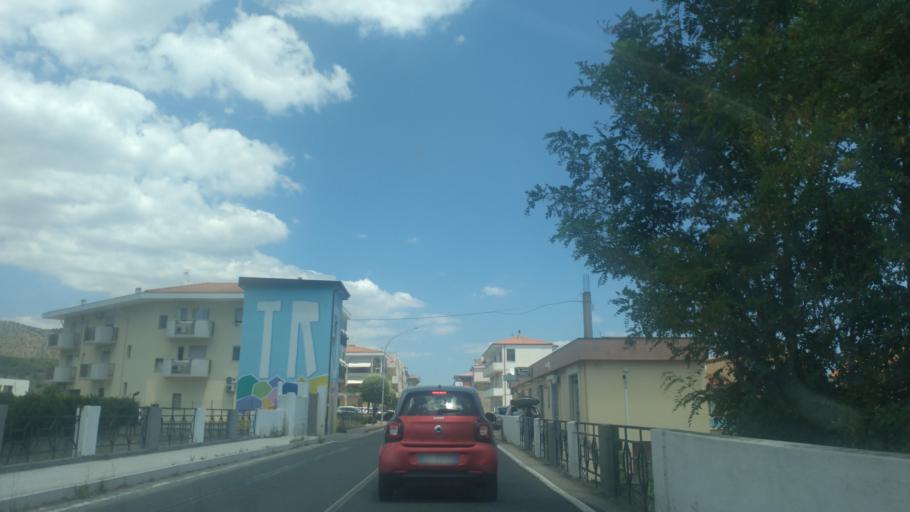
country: IT
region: Calabria
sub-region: Provincia di Catanzaro
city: Montepaone Lido
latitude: 38.7252
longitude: 16.5382
